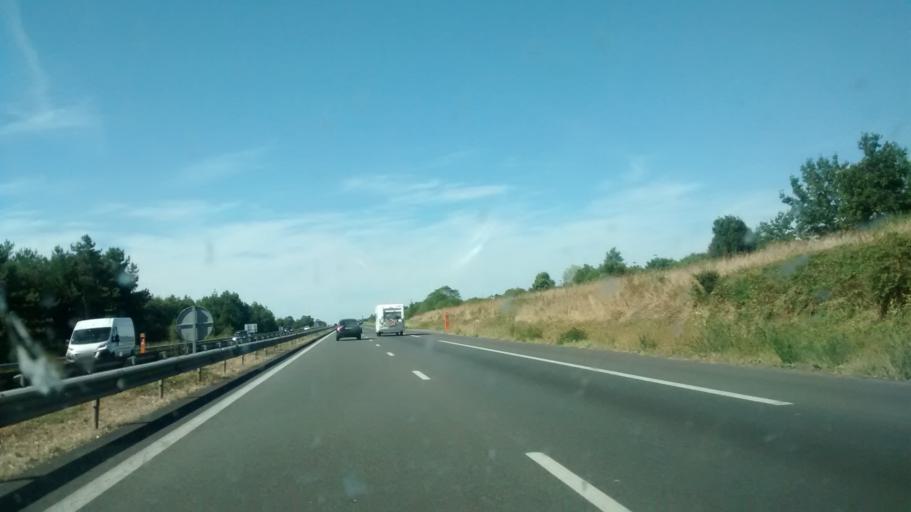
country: FR
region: Pays de la Loire
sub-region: Departement de la Loire-Atlantique
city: Le Bignon
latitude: 47.1198
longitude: -1.4964
